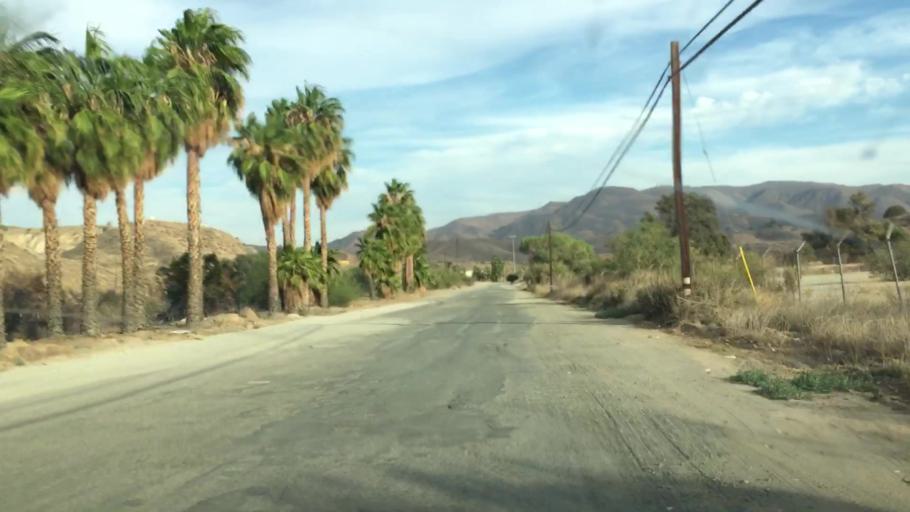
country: US
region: California
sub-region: Riverside County
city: El Cerrito
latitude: 33.7824
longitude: -117.4806
